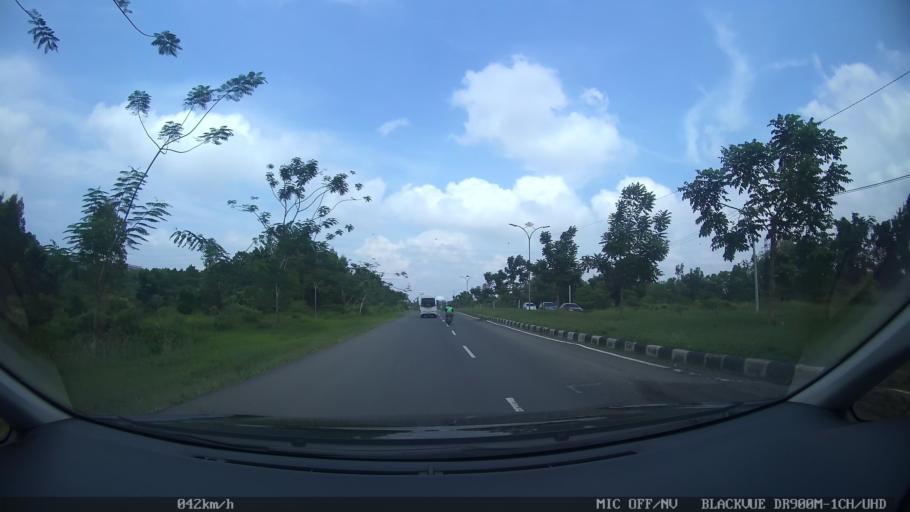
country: ID
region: Lampung
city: Kedaton
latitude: -5.3577
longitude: 105.3110
